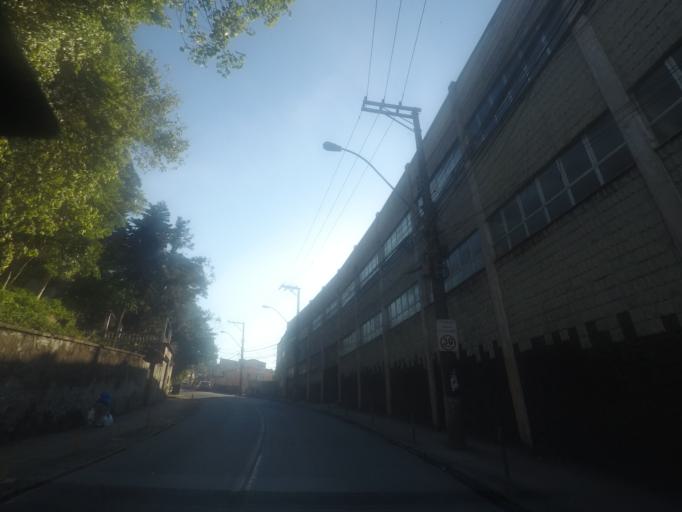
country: BR
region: Rio de Janeiro
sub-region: Petropolis
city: Petropolis
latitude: -22.4899
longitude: -43.1549
